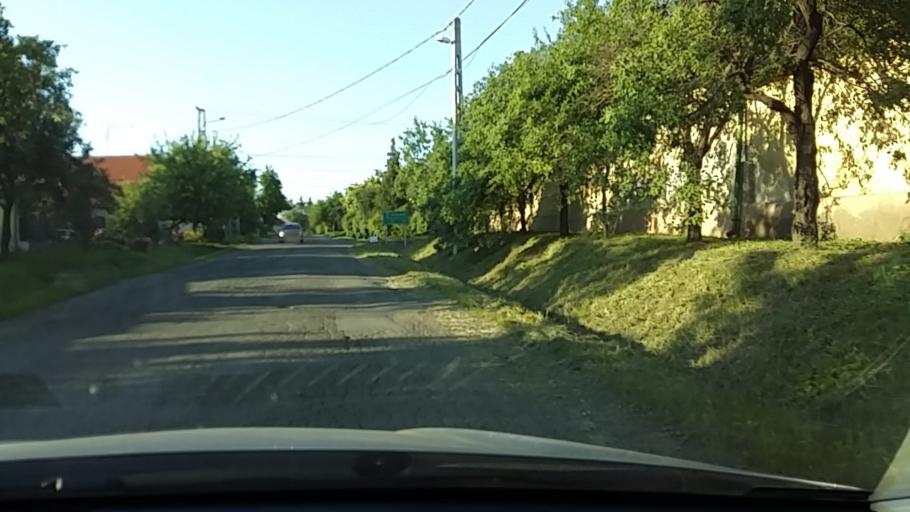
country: HU
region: Nograd
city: Diosjeno
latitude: 47.9094
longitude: 19.0455
